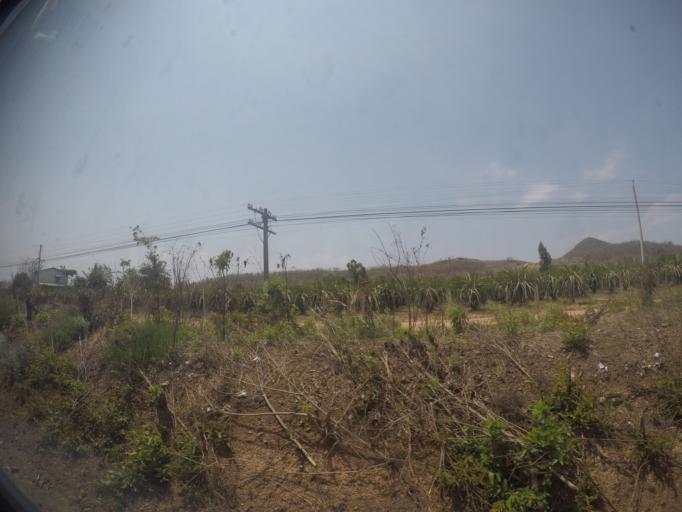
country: VN
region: Binh Thuan
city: Thuan Nam
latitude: 10.9368
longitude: 107.9666
